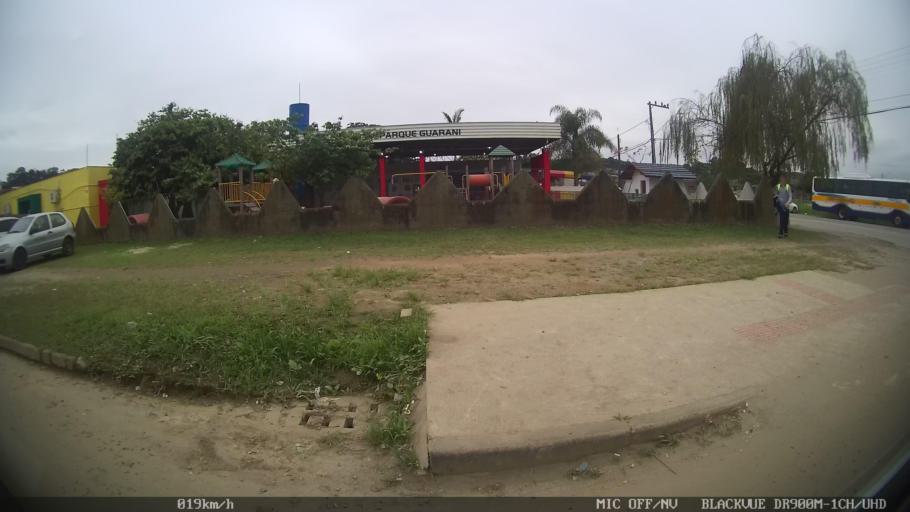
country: BR
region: Santa Catarina
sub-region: Joinville
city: Joinville
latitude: -26.3618
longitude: -48.8129
